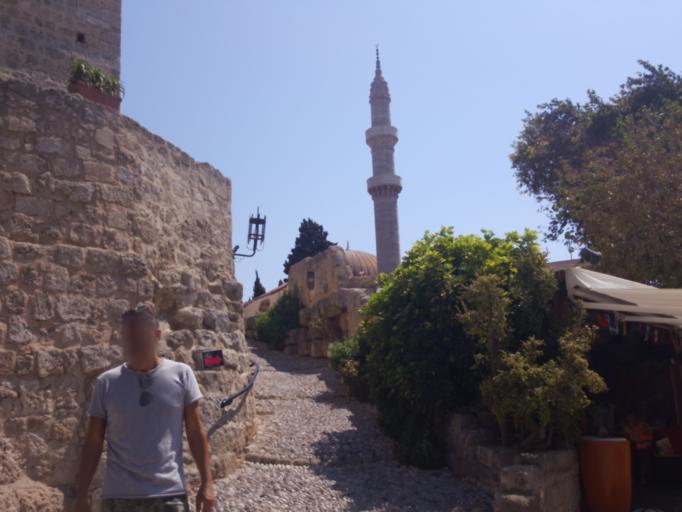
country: GR
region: South Aegean
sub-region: Nomos Dodekanisou
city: Rodos
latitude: 36.4442
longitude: 28.2236
